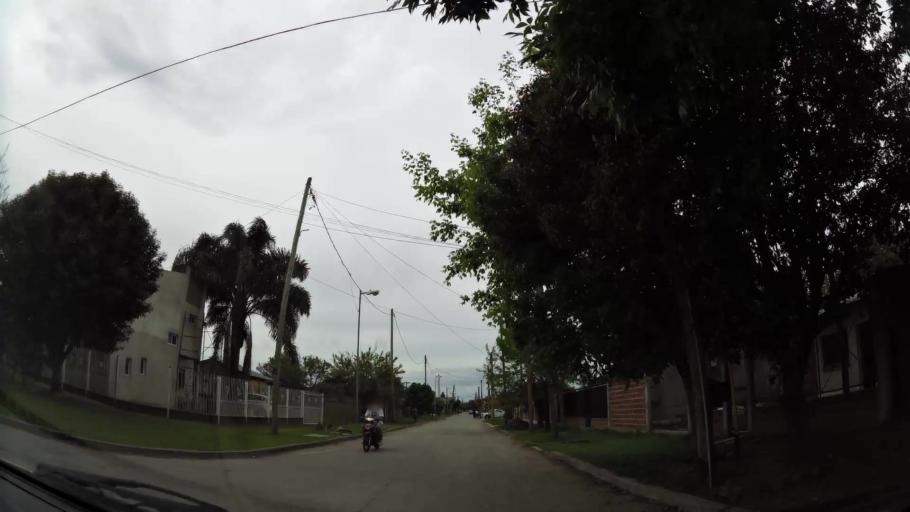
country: AR
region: Buenos Aires
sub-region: Partido de Quilmes
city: Quilmes
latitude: -34.7523
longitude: -58.2540
